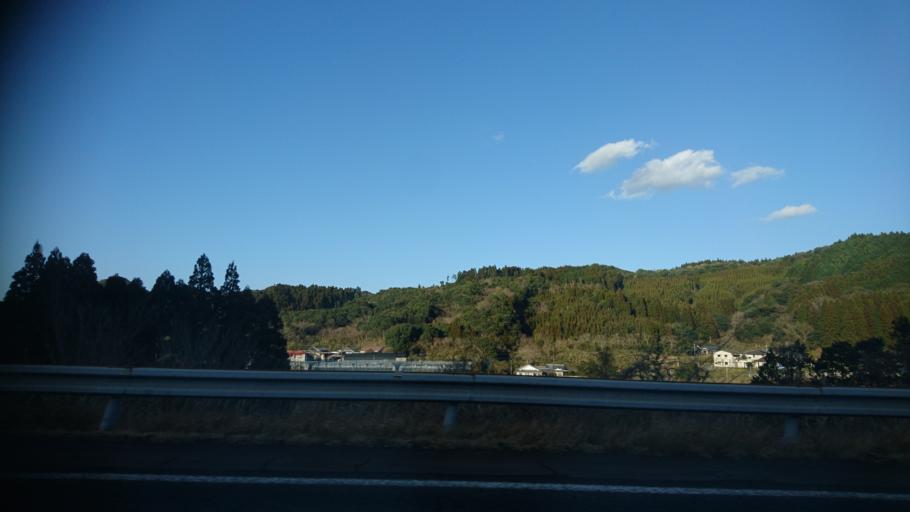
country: JP
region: Miyazaki
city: Miyakonojo
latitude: 31.7936
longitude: 131.1766
